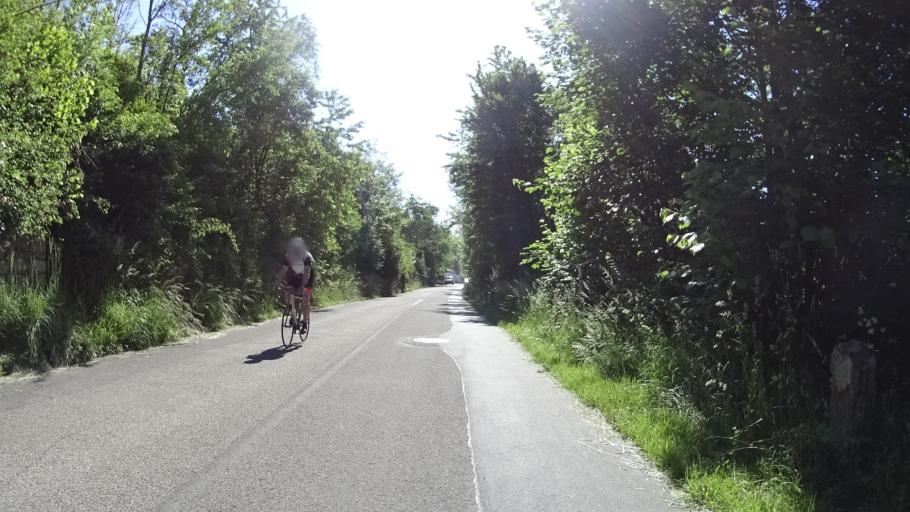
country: DE
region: Baden-Wuerttemberg
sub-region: Regierungsbezirk Stuttgart
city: Bad Mergentheim
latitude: 49.4993
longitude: 9.7647
